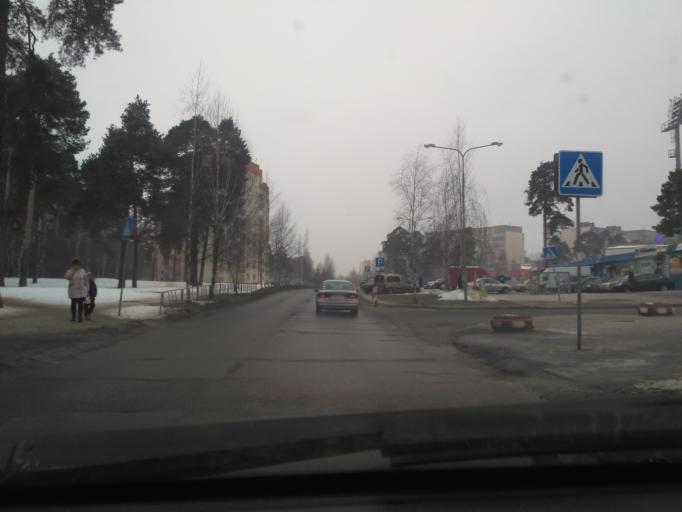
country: BY
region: Minsk
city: Horad Barysaw
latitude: 54.2209
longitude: 28.4892
